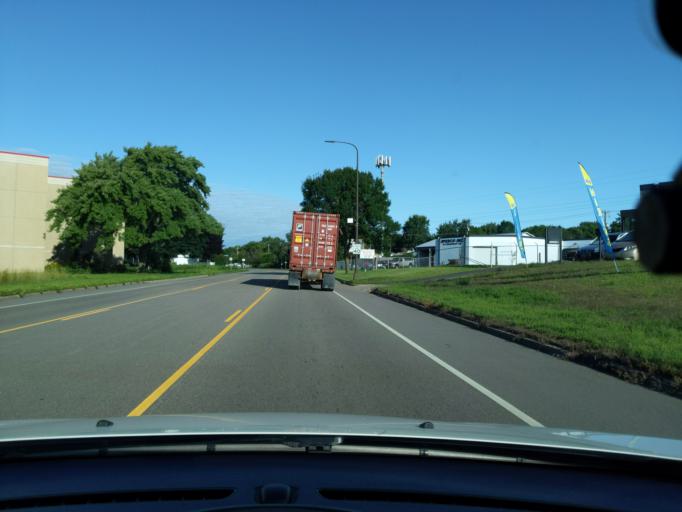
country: US
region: Minnesota
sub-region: Ramsey County
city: Falcon Heights
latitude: 44.9655
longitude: -93.1399
